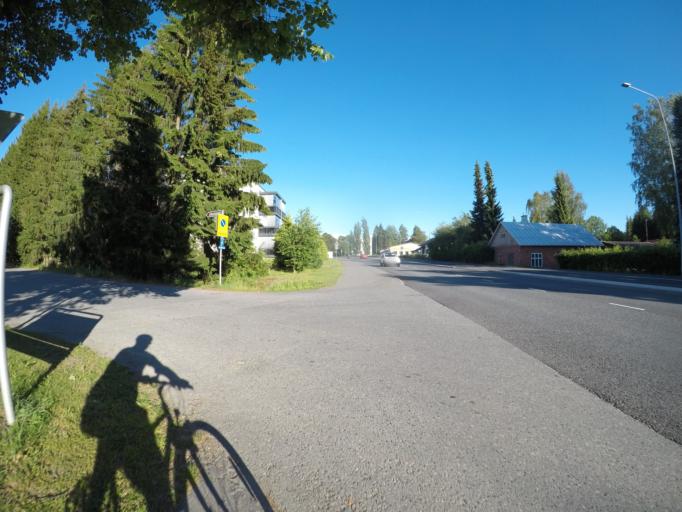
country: FI
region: Haeme
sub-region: Haemeenlinna
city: Haemeenlinna
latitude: 60.9855
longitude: 24.4418
